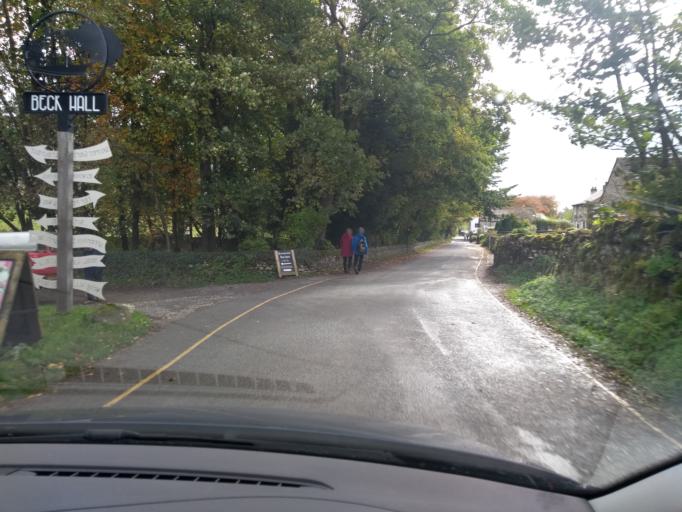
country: GB
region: England
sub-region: North Yorkshire
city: Gargrave
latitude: 54.0633
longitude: -2.1539
